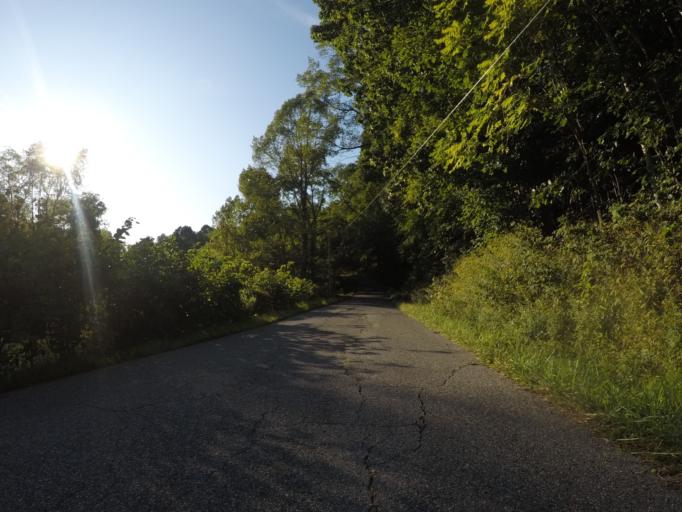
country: US
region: Ohio
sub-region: Lawrence County
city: Burlington
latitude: 38.5270
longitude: -82.5208
